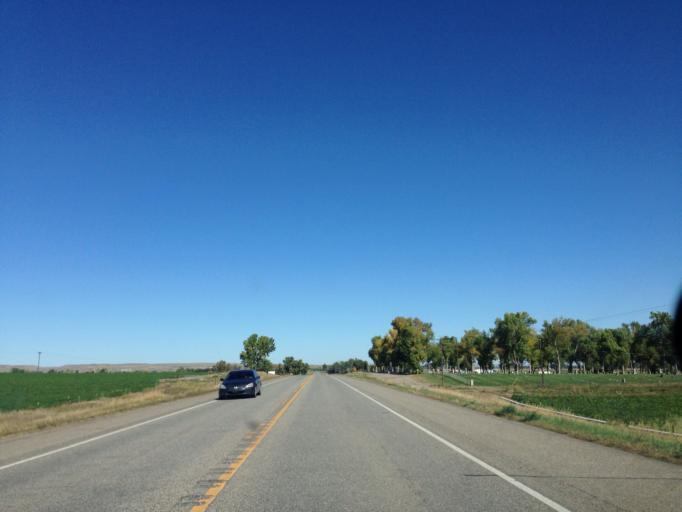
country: US
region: Montana
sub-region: Yellowstone County
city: Laurel
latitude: 45.4860
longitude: -108.8631
